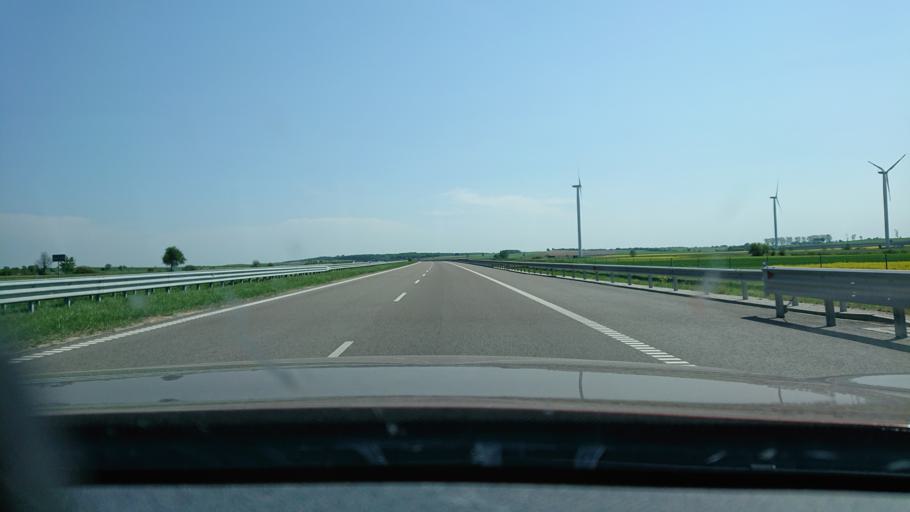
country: PL
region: Subcarpathian Voivodeship
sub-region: Powiat przemyski
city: Stubno
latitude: 49.9435
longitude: 22.9997
